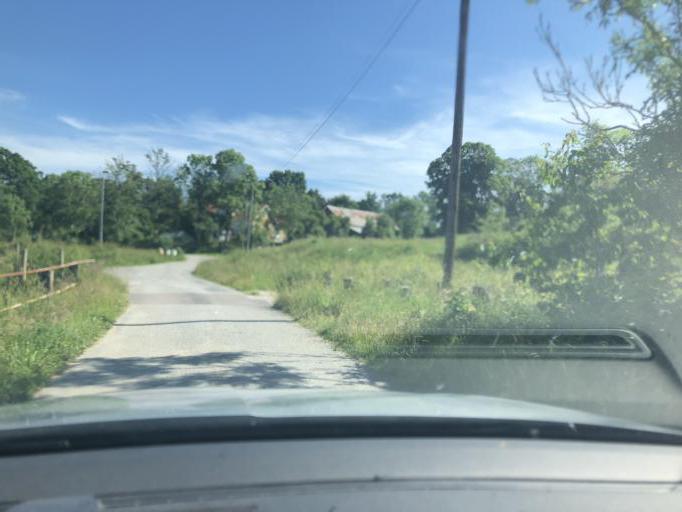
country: SE
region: Blekinge
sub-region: Karlshamns Kommun
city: Morrum
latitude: 56.1865
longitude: 14.7006
